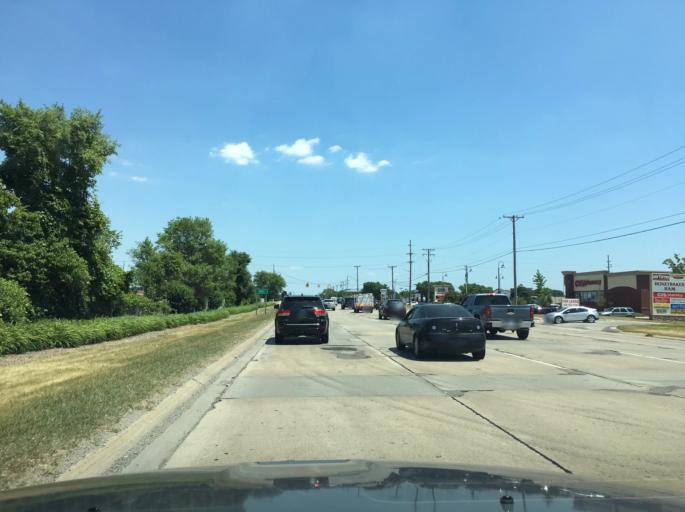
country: US
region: Michigan
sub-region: Macomb County
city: Utica
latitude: 42.6271
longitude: -82.9756
